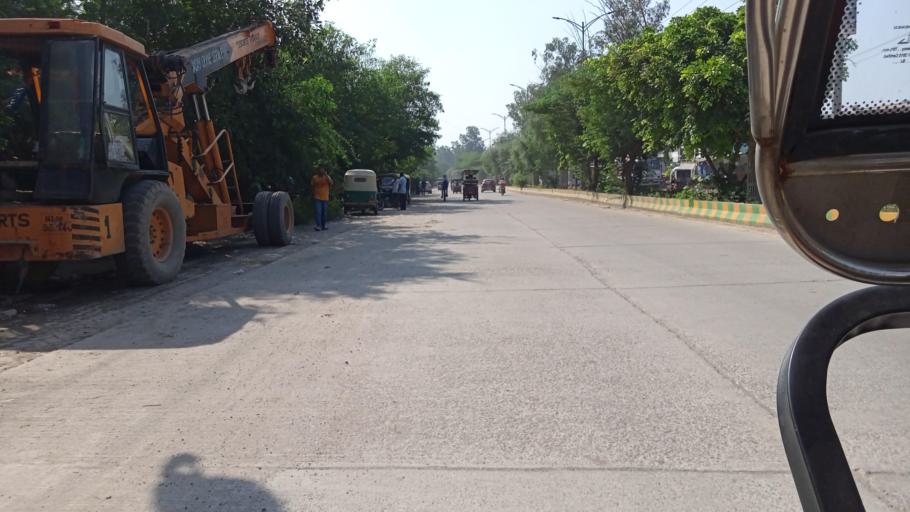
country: IN
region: Uttar Pradesh
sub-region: Ghaziabad
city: Ghaziabad
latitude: 28.6712
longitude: 77.3611
